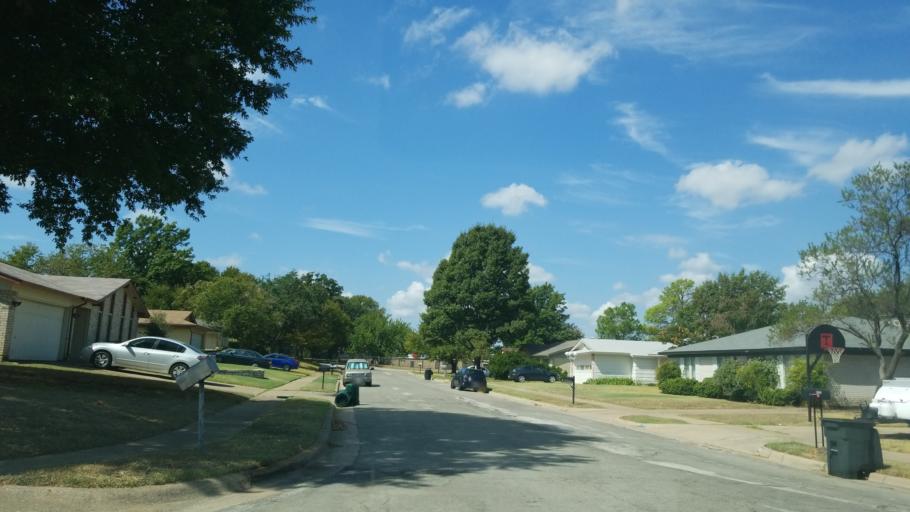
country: US
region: Texas
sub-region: Tarrant County
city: Euless
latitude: 32.8595
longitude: -97.0916
